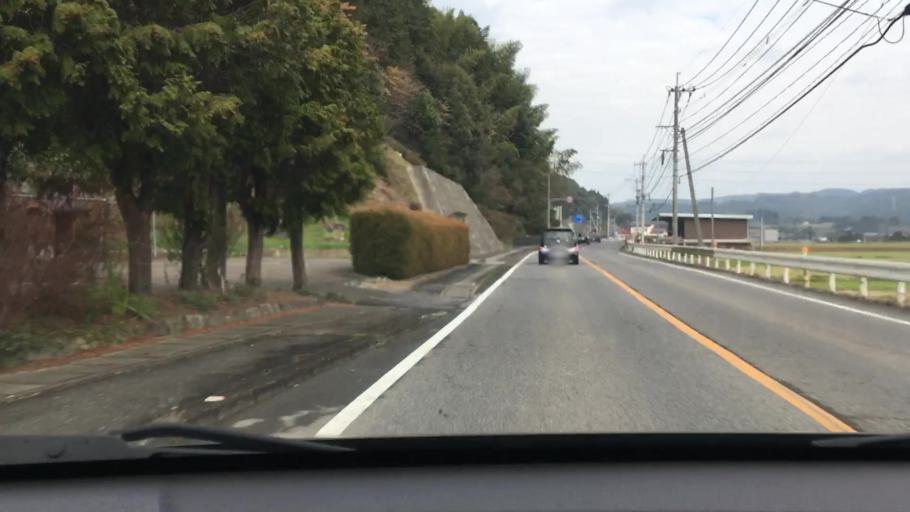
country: JP
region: Saga Prefecture
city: Imaricho-ko
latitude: 33.3018
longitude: 129.9199
